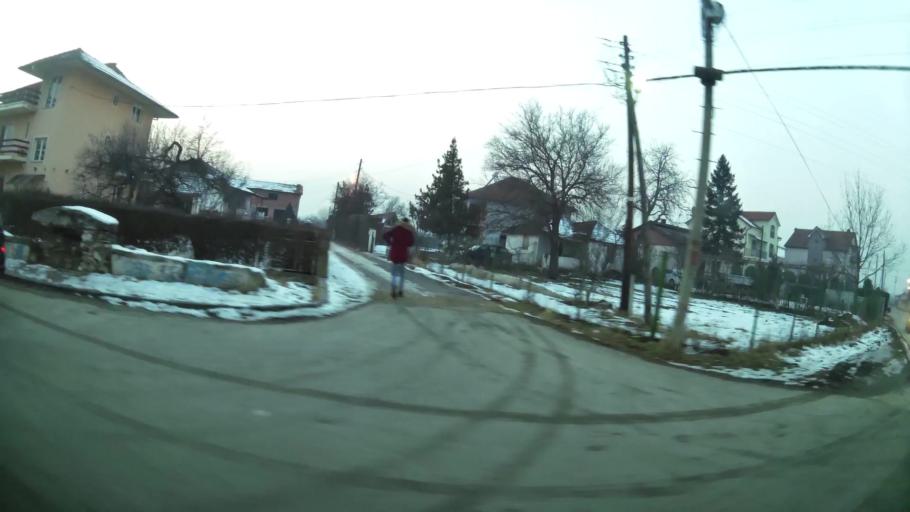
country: MK
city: Creshevo
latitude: 42.0057
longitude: 21.5177
